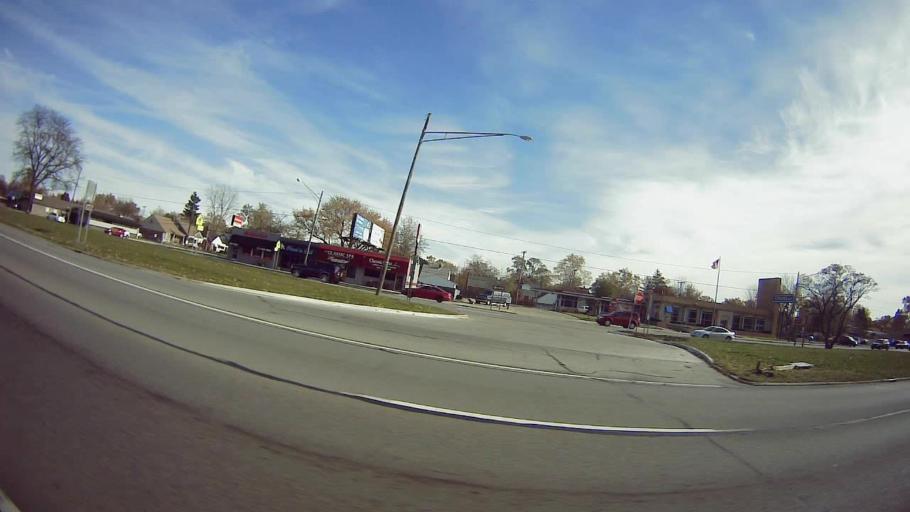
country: US
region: Michigan
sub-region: Wayne County
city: Dearborn Heights
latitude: 42.3184
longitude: -83.2725
